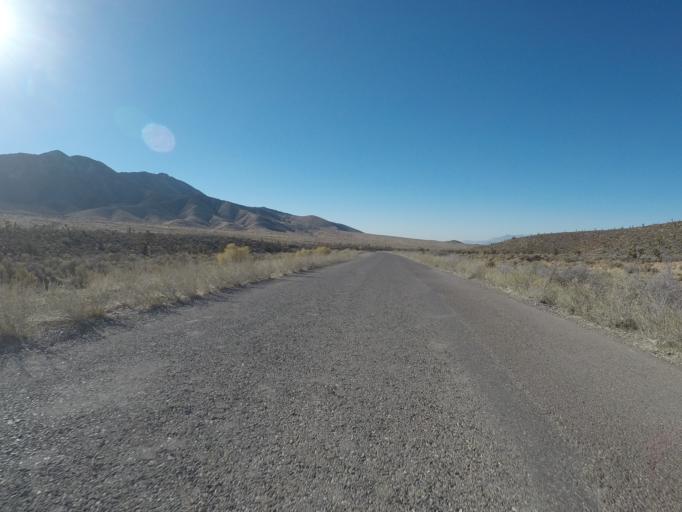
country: US
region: Nevada
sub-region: Clark County
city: Sandy Valley
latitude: 36.0220
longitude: -115.5613
